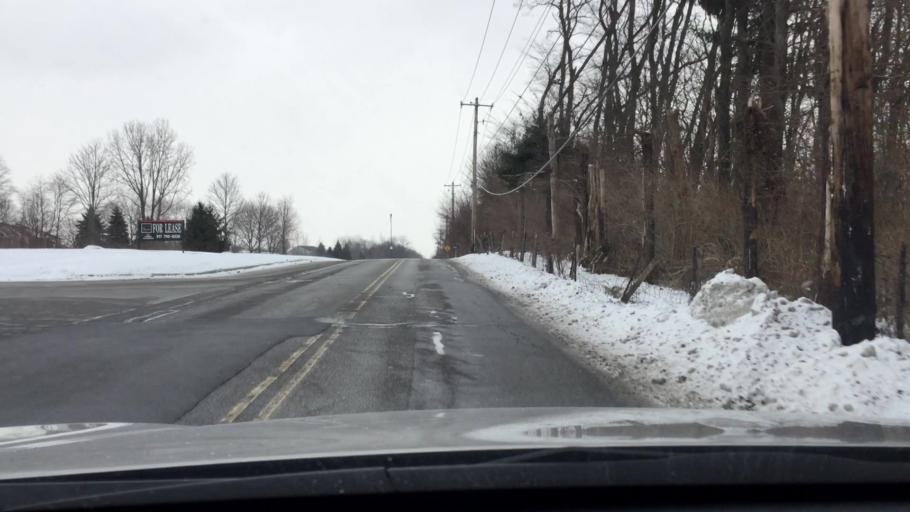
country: US
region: Indiana
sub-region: Hamilton County
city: Fishers
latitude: 39.9643
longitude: -85.9891
